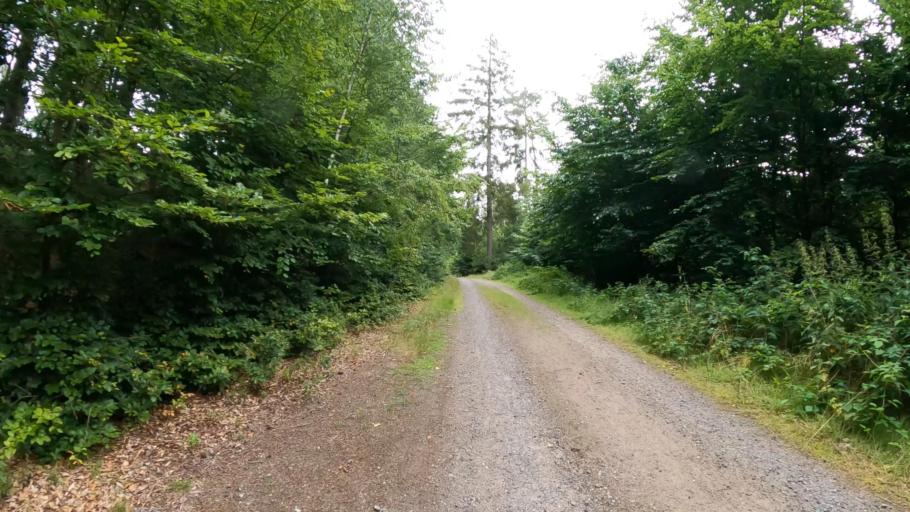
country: DE
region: Schleswig-Holstein
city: Wittenborn
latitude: 53.9307
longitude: 10.2097
